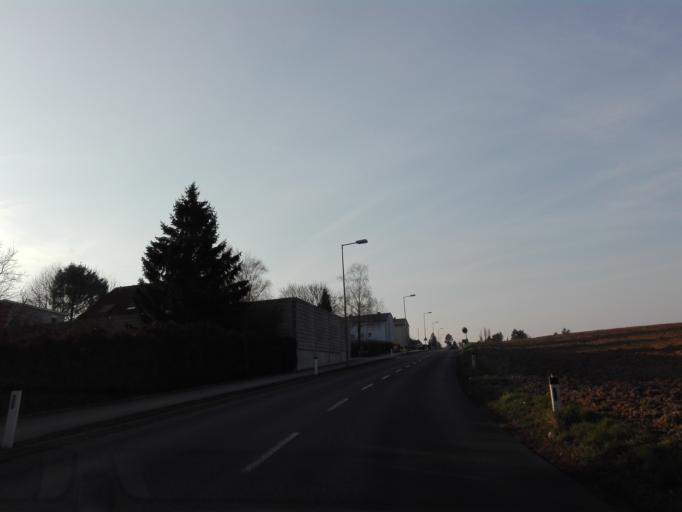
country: AT
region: Upper Austria
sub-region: Politischer Bezirk Linz-Land
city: Horsching
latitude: 48.2210
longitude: 14.1861
